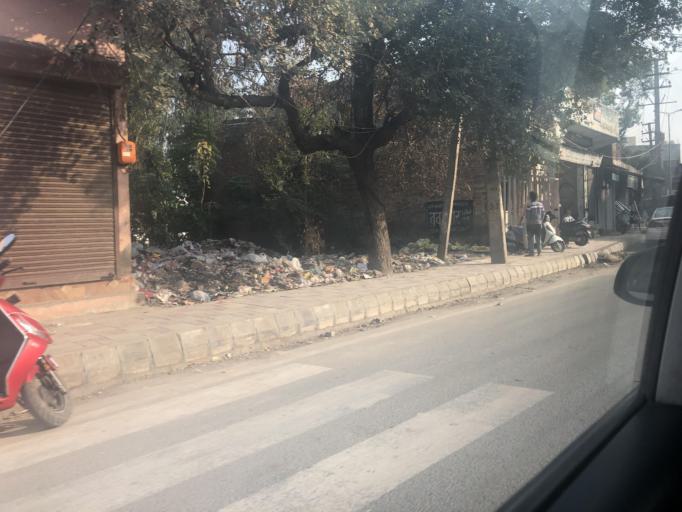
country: IN
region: Haryana
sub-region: Jhajjar
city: Bahadurgarh
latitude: 28.6170
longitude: 76.9754
